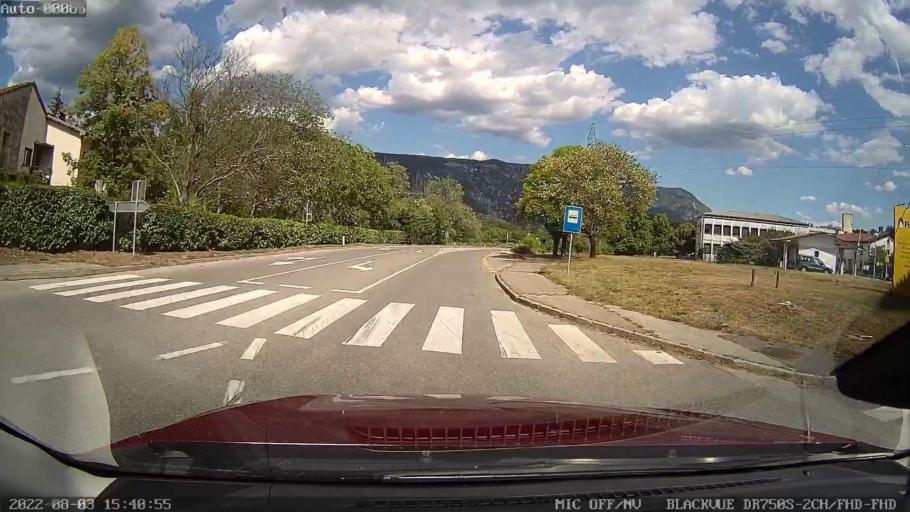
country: SI
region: Nova Gorica
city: Kromberk
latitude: 45.9568
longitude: 13.6783
